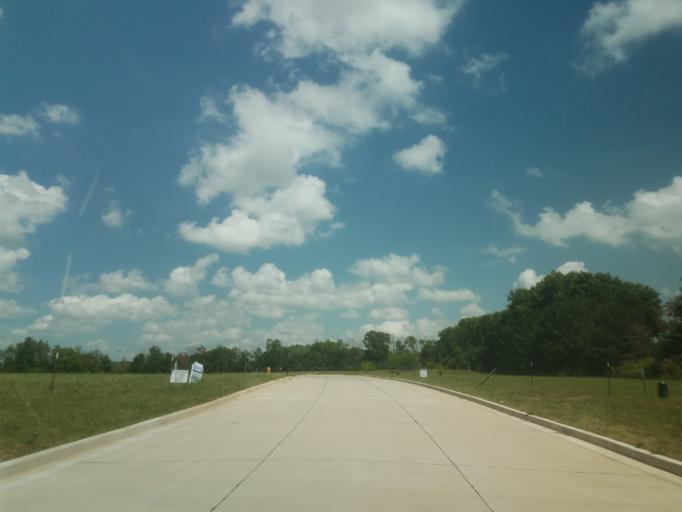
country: US
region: Illinois
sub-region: McLean County
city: Bloomington
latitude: 40.4477
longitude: -89.0320
